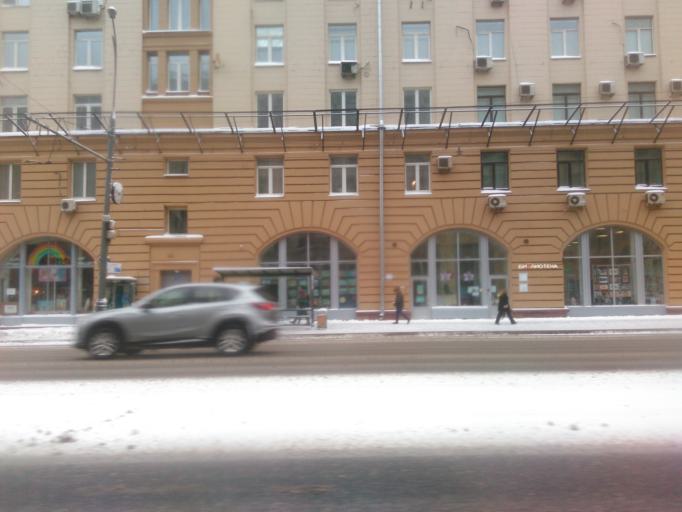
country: RU
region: Moscow
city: Mar'ina Roshcha
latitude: 55.7871
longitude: 37.6352
